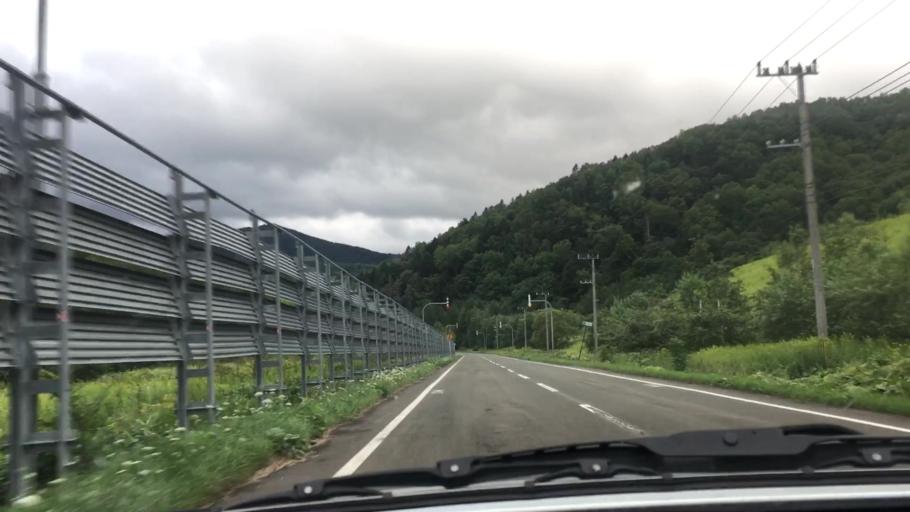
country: JP
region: Hokkaido
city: Shimo-furano
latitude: 43.0579
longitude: 142.5306
